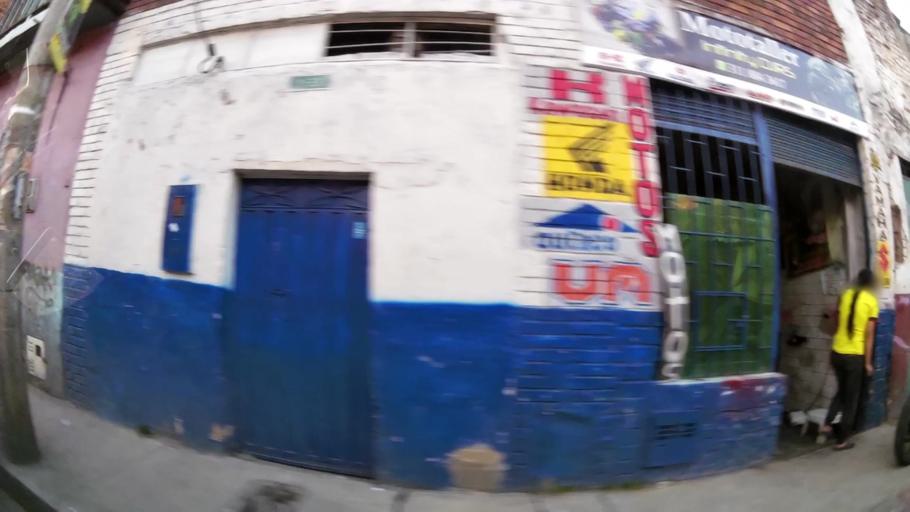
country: CO
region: Bogota D.C.
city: Bogota
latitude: 4.5864
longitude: -74.0809
